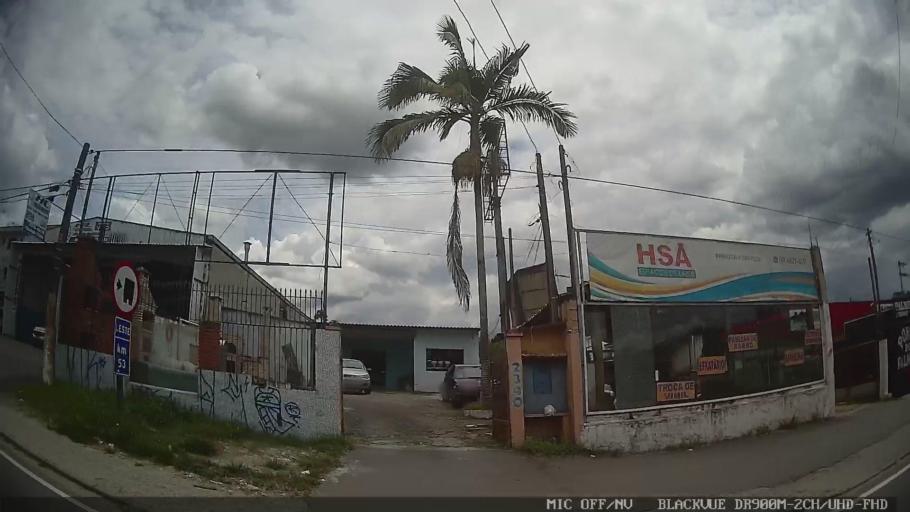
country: BR
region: Sao Paulo
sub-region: Ribeirao Pires
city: Ribeirao Pires
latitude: -23.6813
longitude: -46.3595
